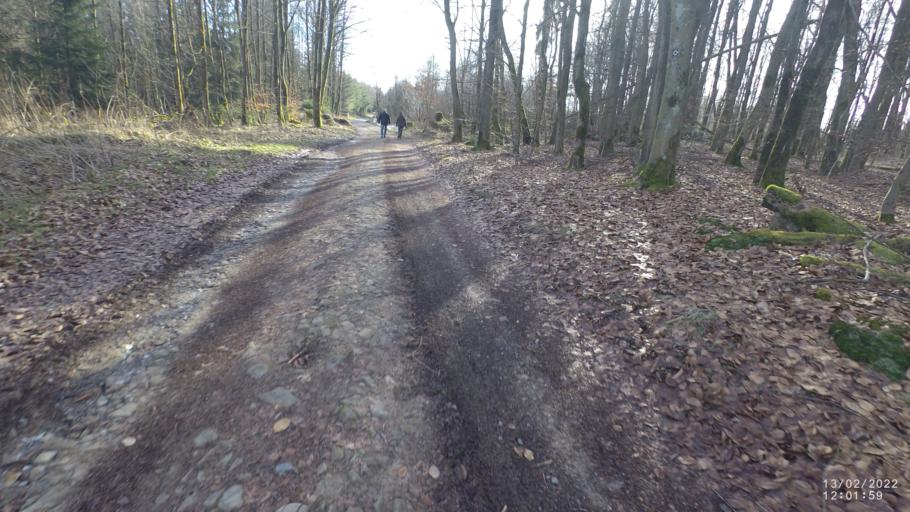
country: DE
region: North Rhine-Westphalia
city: Neuenrade
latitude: 51.3081
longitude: 7.7612
